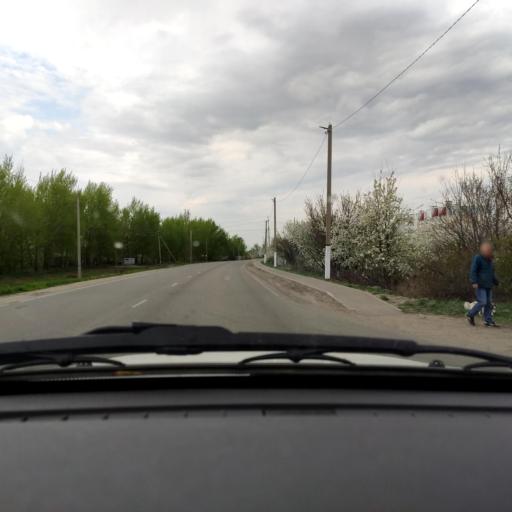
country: RU
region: Voronezj
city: Novaya Usman'
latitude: 51.6059
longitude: 39.3733
